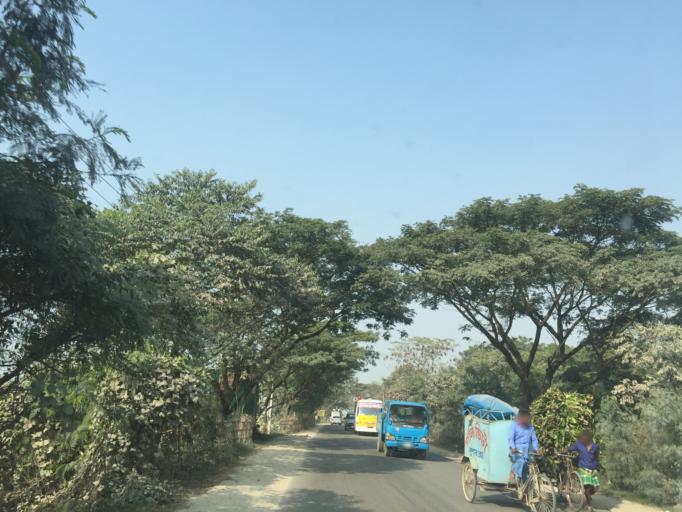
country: BD
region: Dhaka
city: Tungi
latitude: 23.8345
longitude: 90.3401
